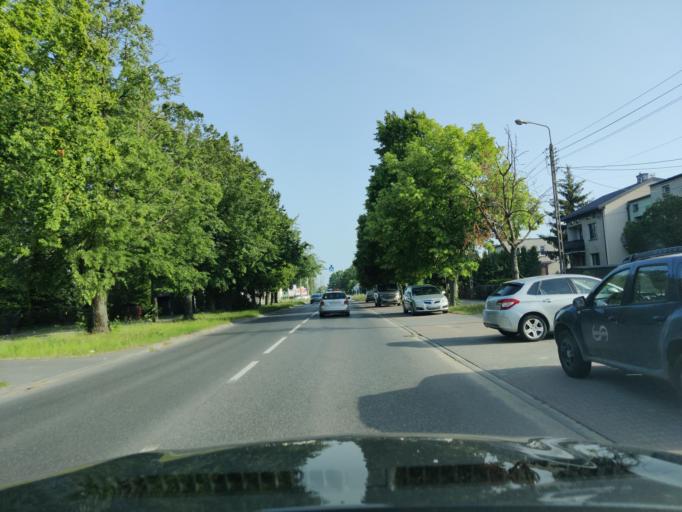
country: PL
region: Masovian Voivodeship
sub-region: Powiat wyszkowski
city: Wyszkow
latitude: 52.6048
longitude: 21.4550
